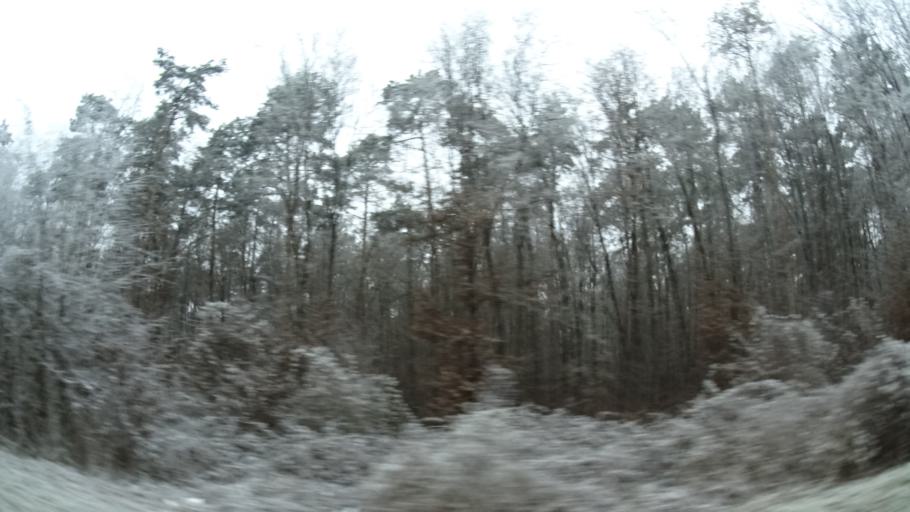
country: DE
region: Bavaria
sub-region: Regierungsbezirk Unterfranken
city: Albertshofen
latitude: 49.7748
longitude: 10.2029
